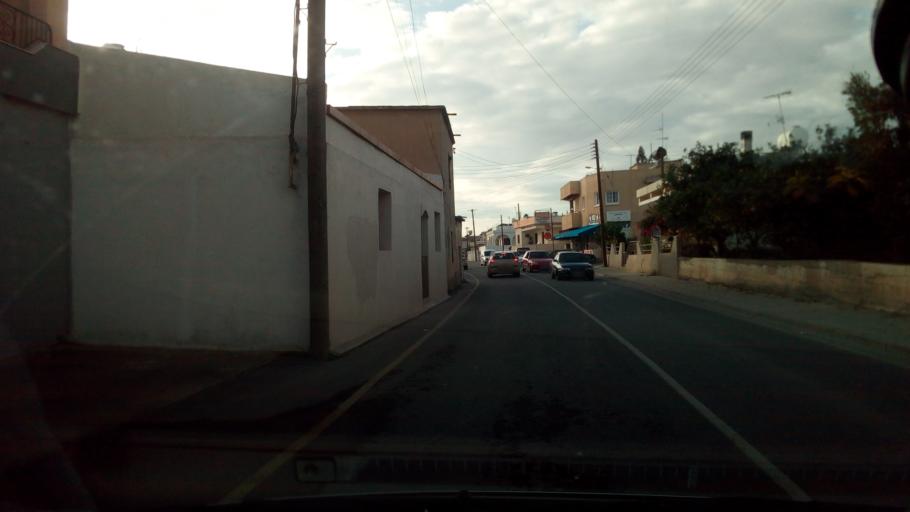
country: CY
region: Larnaka
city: Xylotymbou
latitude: 34.9926
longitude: 33.7772
